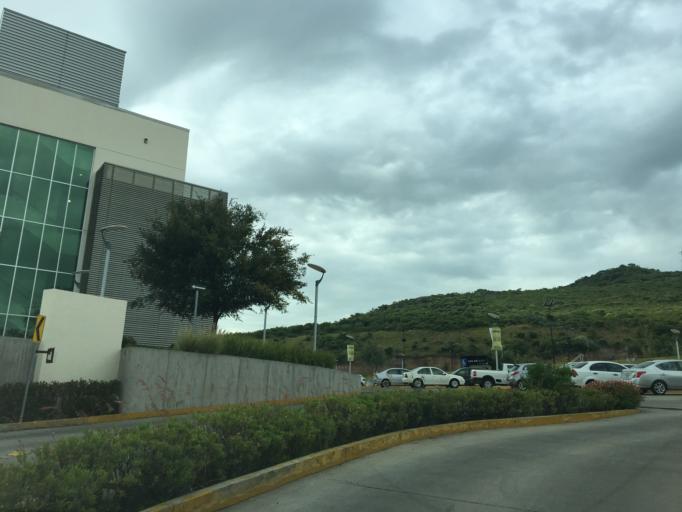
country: MX
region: Guanajuato
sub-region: Leon
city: La Ermita
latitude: 21.1662
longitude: -101.7128
